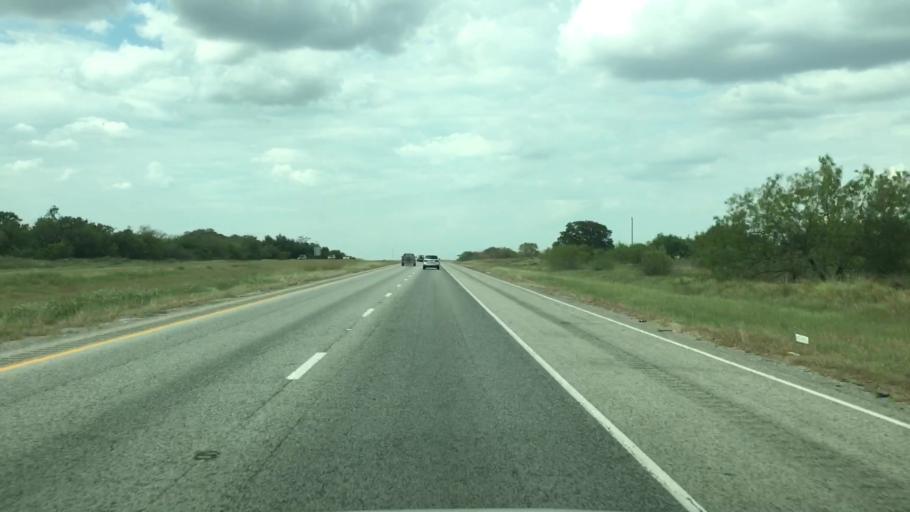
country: US
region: Texas
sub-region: Atascosa County
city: Pleasanton
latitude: 29.0601
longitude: -98.4325
